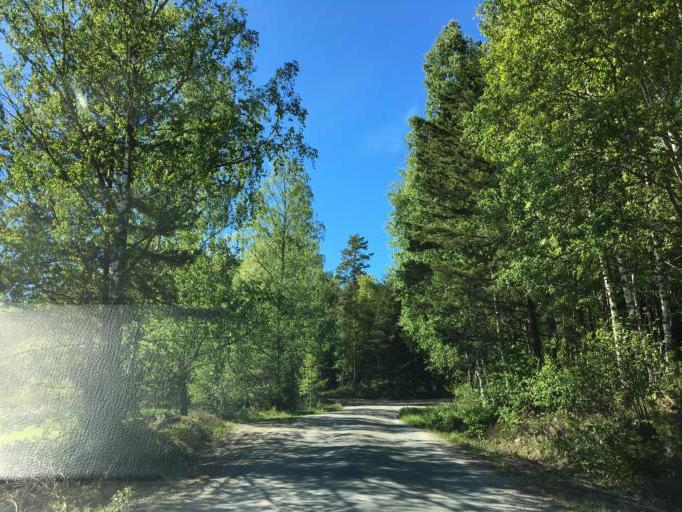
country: SE
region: Soedermanland
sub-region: Eskilstuna Kommun
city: Hallbybrunn
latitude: 59.3549
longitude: 16.3604
